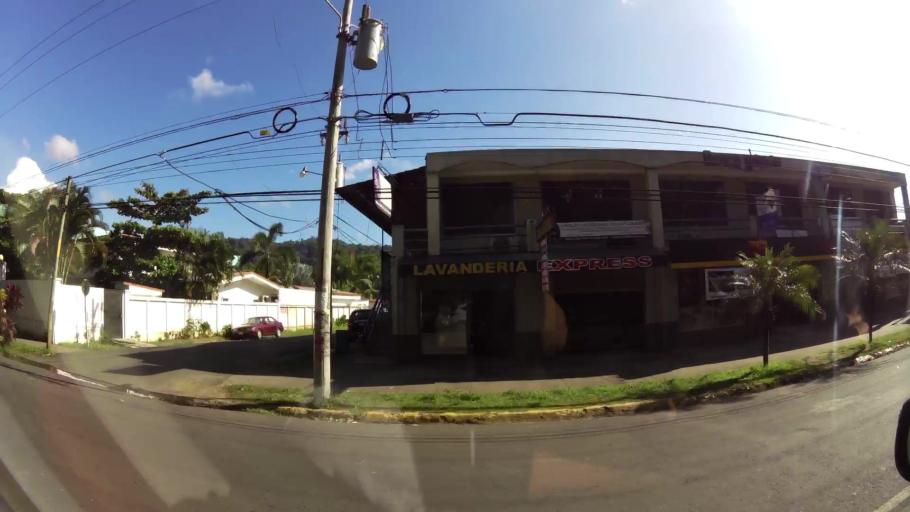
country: CR
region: Puntarenas
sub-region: Canton de Garabito
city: Jaco
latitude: 9.6112
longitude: -84.6191
